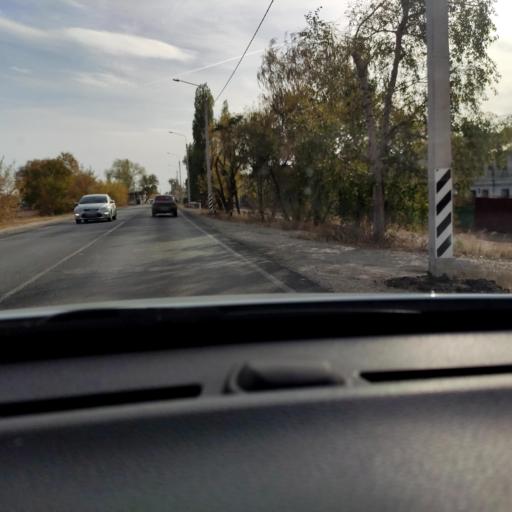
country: RU
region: Voronezj
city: Maslovka
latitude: 51.5684
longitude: 39.2460
